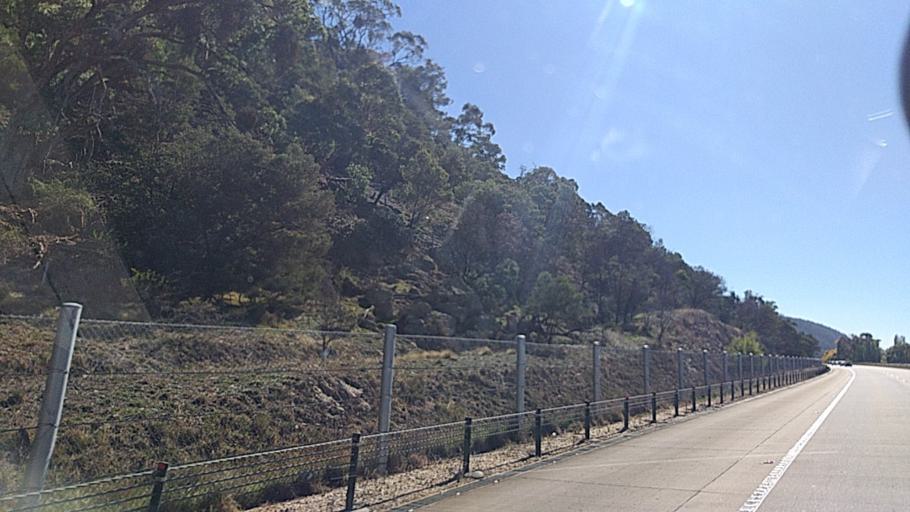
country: AU
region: New South Wales
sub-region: Yass Valley
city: Gundaroo
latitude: -35.0786
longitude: 149.3744
